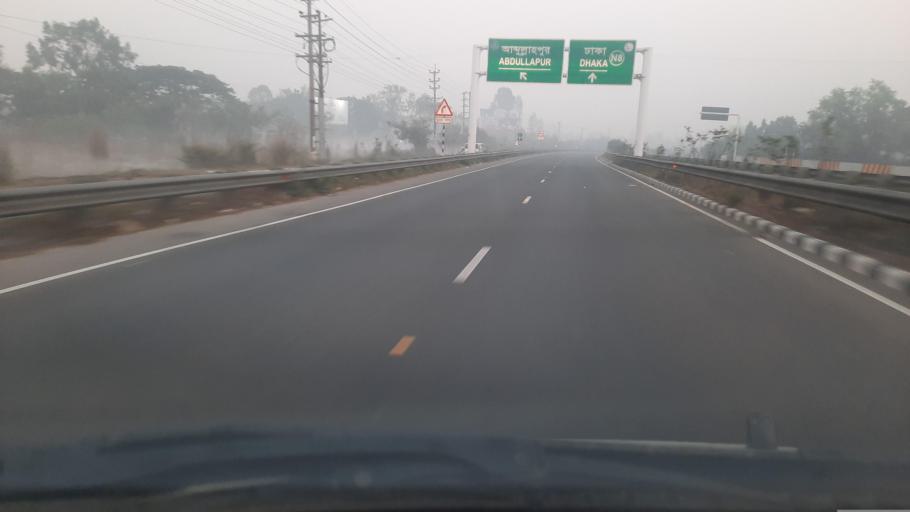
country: BD
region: Dhaka
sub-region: Dhaka
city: Dhaka
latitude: 23.6541
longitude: 90.3510
